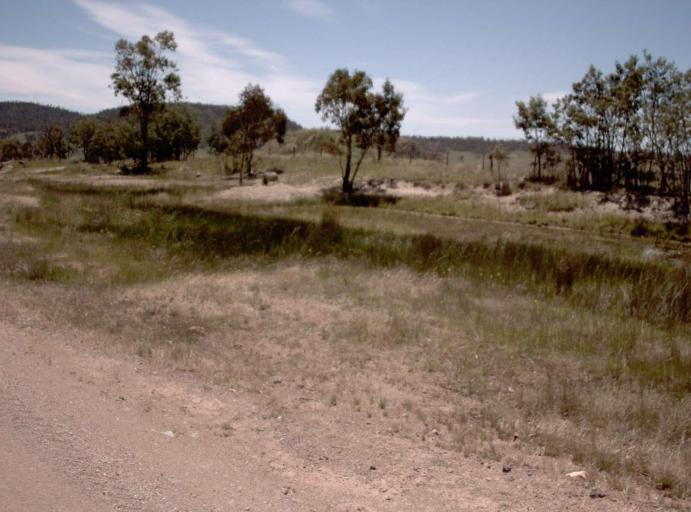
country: AU
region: New South Wales
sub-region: Snowy River
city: Jindabyne
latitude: -37.0228
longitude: 148.2741
